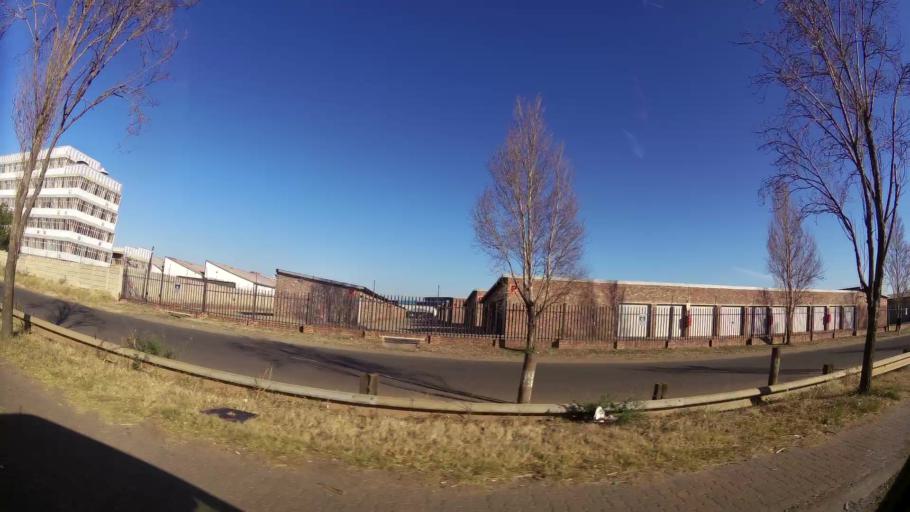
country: ZA
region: Gauteng
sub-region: Ekurhuleni Metropolitan Municipality
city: Germiston
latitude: -26.2914
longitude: 28.1377
